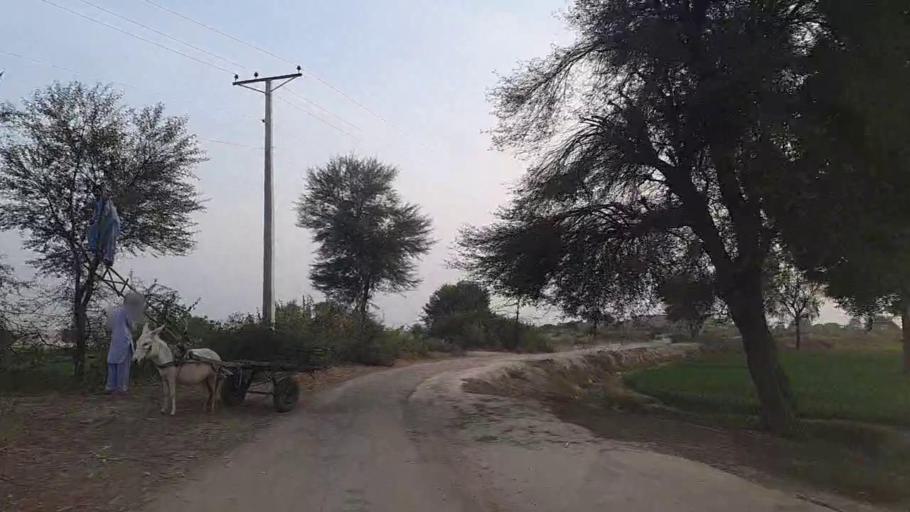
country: PK
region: Sindh
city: Jam Sahib
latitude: 26.4623
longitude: 68.5522
